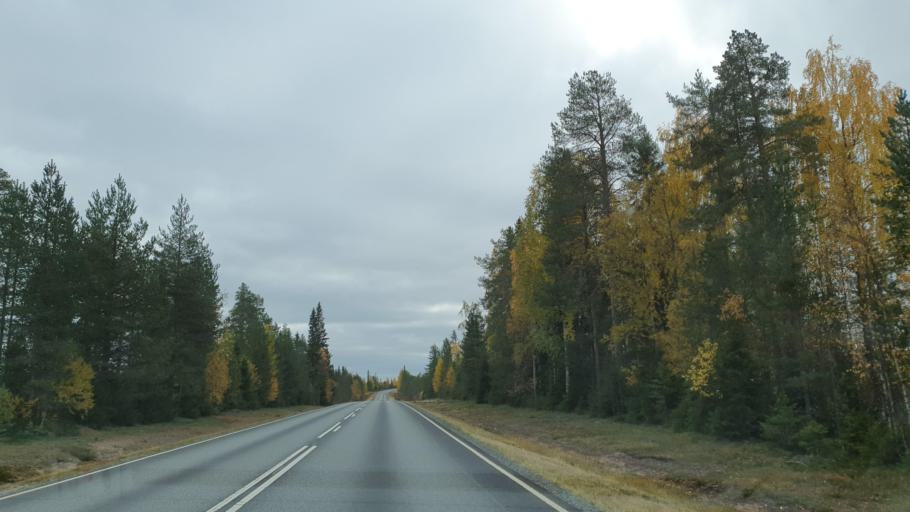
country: FI
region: Lapland
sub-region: Rovaniemi
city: Ranua
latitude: 65.8068
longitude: 26.5610
